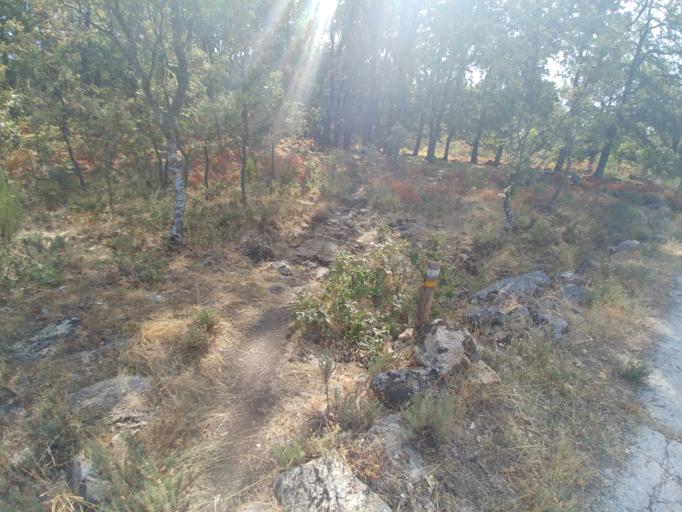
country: ES
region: Extremadura
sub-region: Provincia de Caceres
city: Garganta la Olla
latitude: 40.1085
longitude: -5.7652
